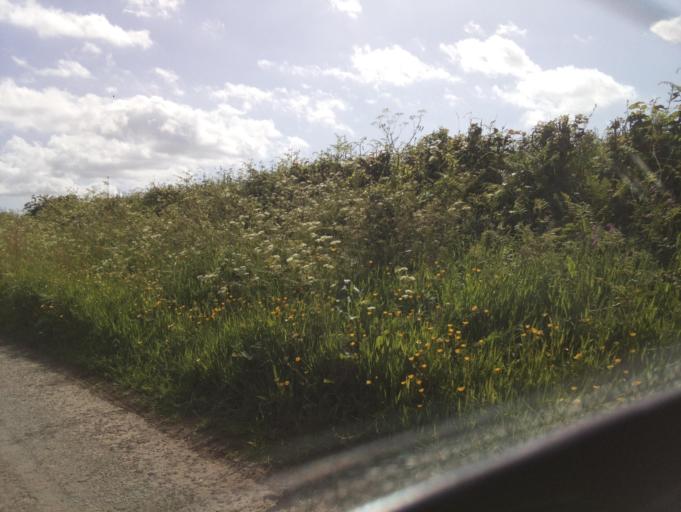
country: GB
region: England
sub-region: Devon
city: Totnes
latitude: 50.4095
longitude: -3.7007
